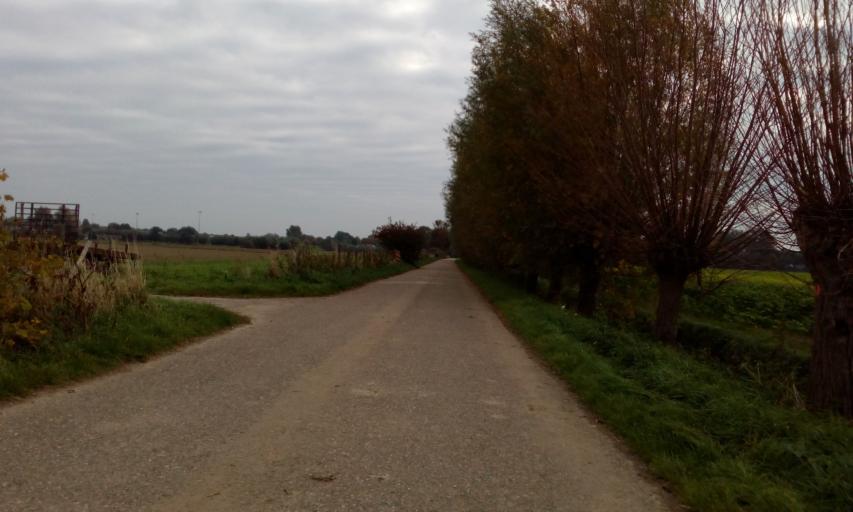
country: NL
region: South Holland
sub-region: Gemeente Albrandswaard
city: Rhoon
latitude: 51.8505
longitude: 4.3885
